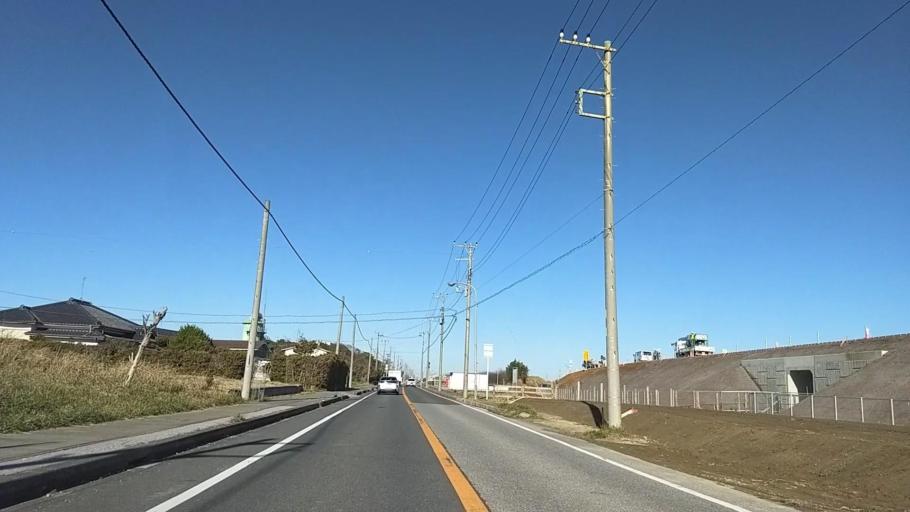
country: JP
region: Chiba
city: Togane
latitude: 35.4575
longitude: 140.4061
